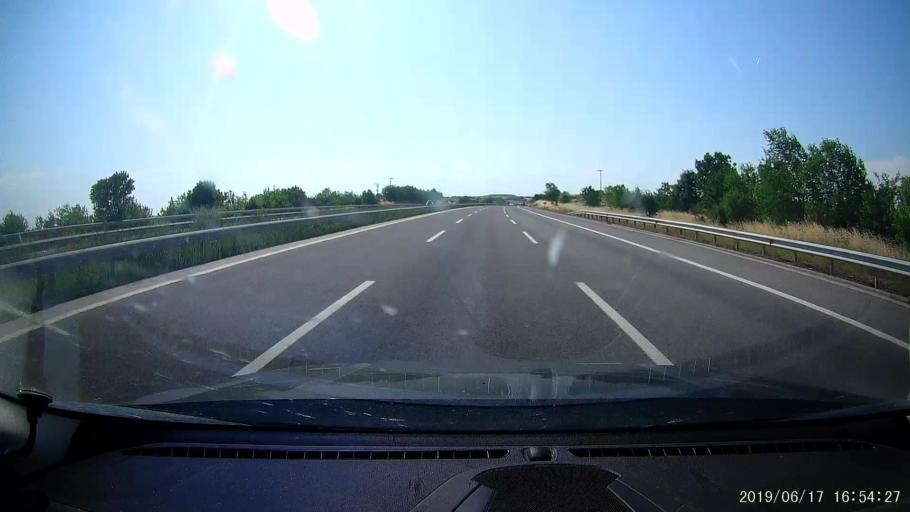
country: TR
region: Kirklareli
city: Inece
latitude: 41.5736
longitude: 26.9955
